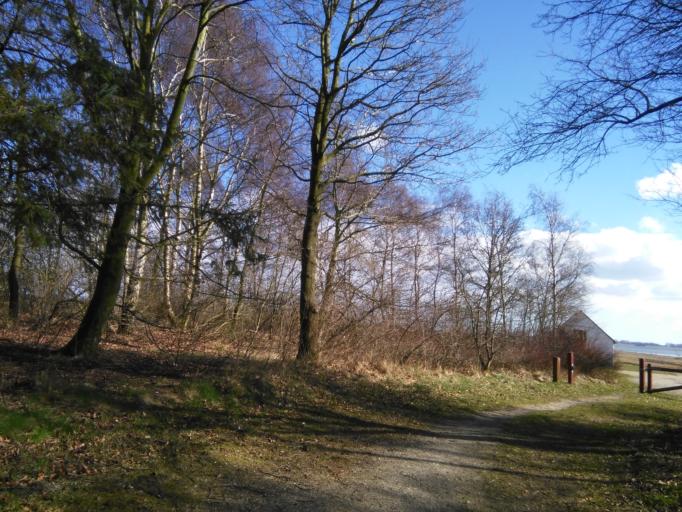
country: DK
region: Central Jutland
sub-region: Horsens Kommune
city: Horsens
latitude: 55.8771
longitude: 10.0096
